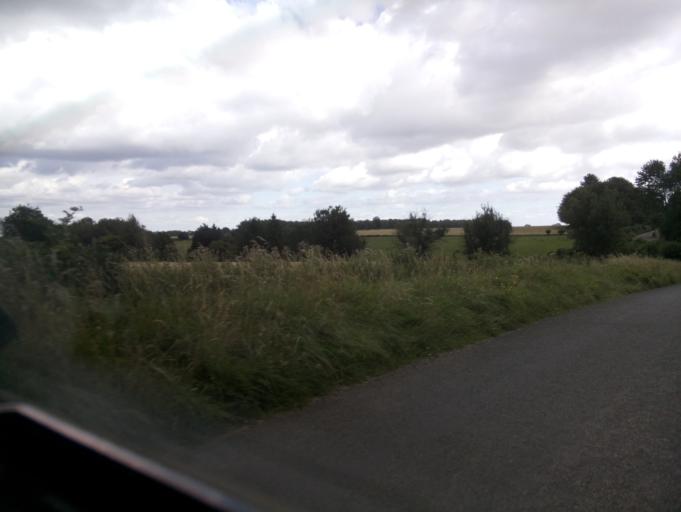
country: GB
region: England
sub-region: Gloucestershire
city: Chalford
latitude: 51.7664
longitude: -2.0902
